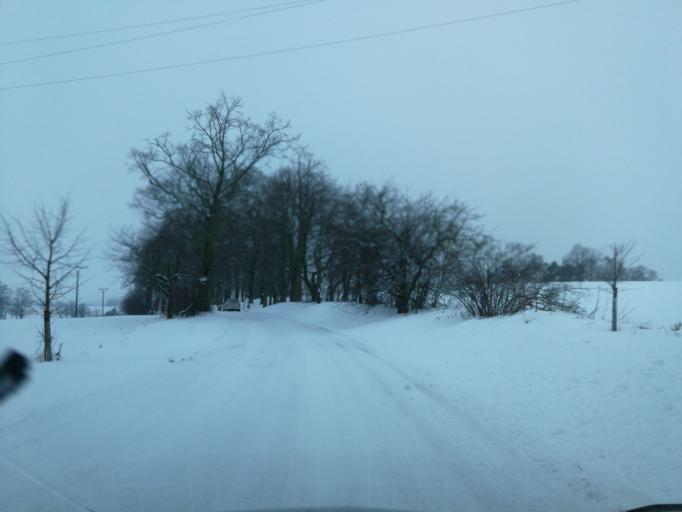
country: CZ
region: Vysocina
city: Heralec
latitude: 49.5283
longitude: 15.4691
